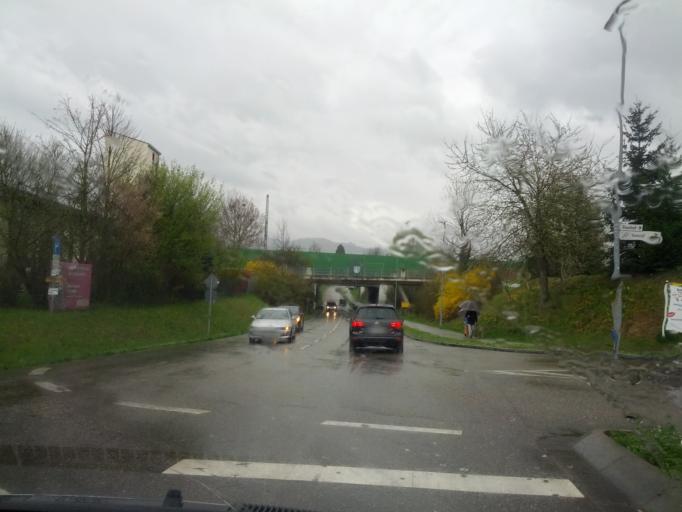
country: DE
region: Baden-Wuerttemberg
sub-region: Freiburg Region
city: Bad Krozingen
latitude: 47.9237
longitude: 7.7009
